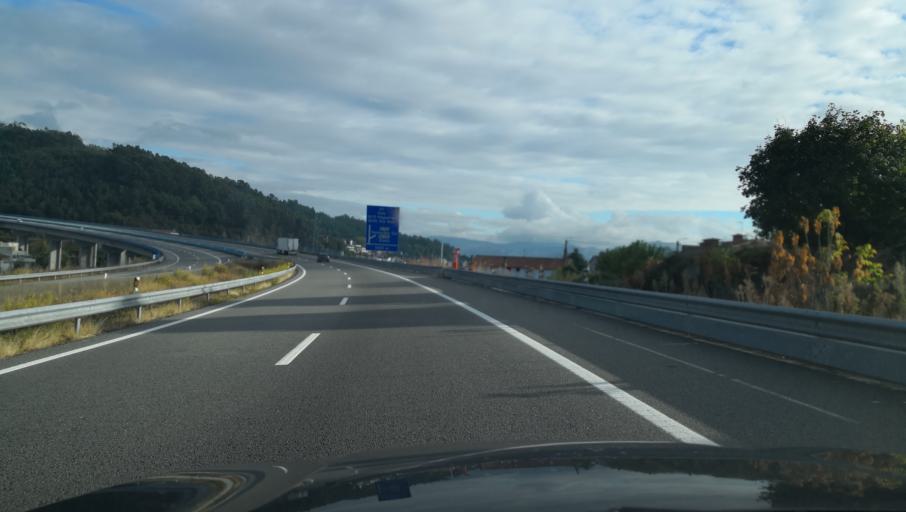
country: PT
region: Braga
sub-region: Guimaraes
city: Candoso
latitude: 41.4118
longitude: -8.3242
